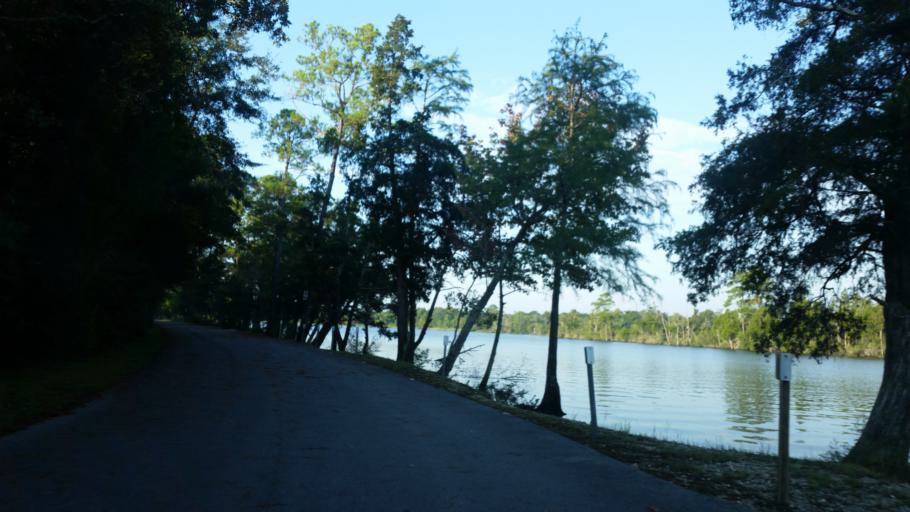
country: US
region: Florida
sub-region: Santa Rosa County
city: Milton
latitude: 30.6304
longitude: -87.0308
